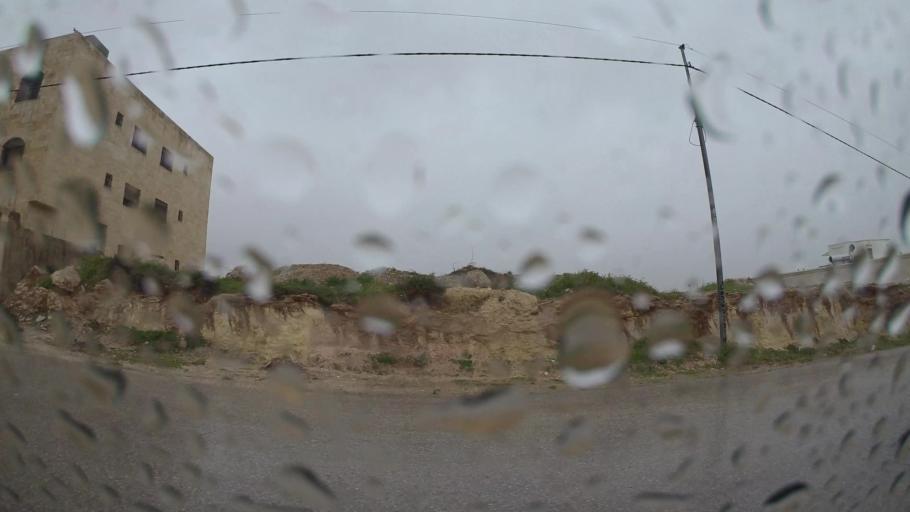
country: JO
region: Amman
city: Al Jubayhah
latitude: 32.0124
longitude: 35.9001
